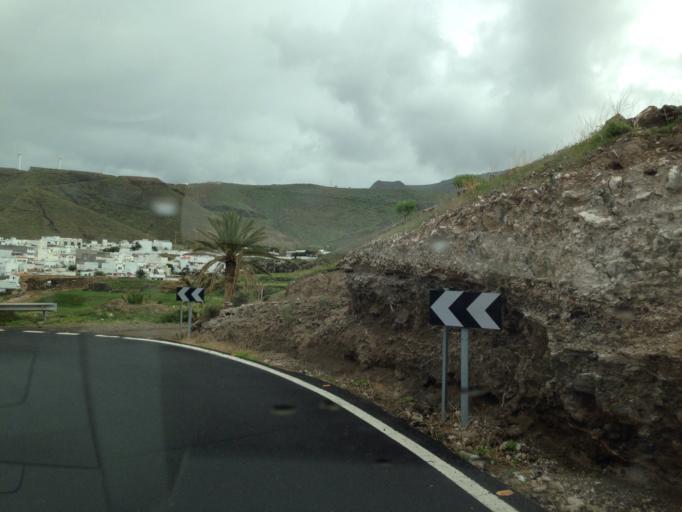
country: ES
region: Canary Islands
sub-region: Provincia de Las Palmas
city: Agaete
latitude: 28.0958
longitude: -15.6994
